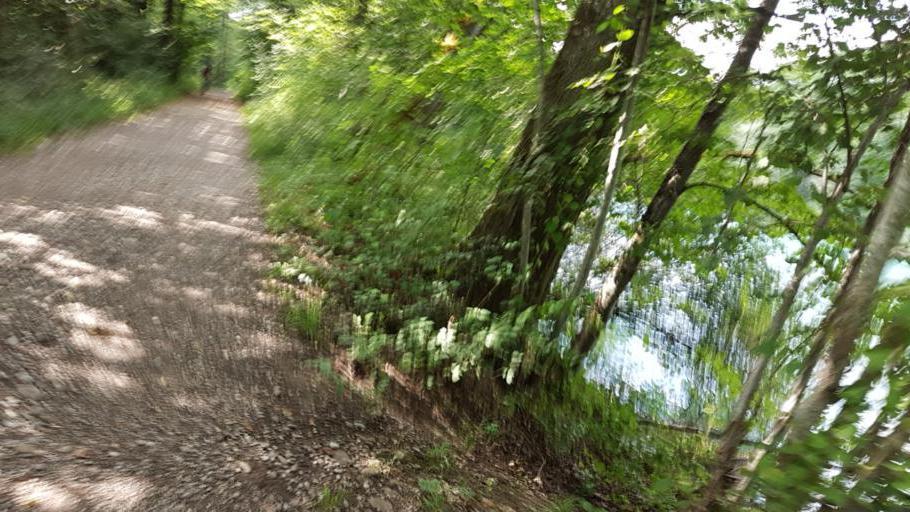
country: CH
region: Bern
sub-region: Bern-Mittelland District
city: Belp
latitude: 46.9062
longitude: 7.5180
